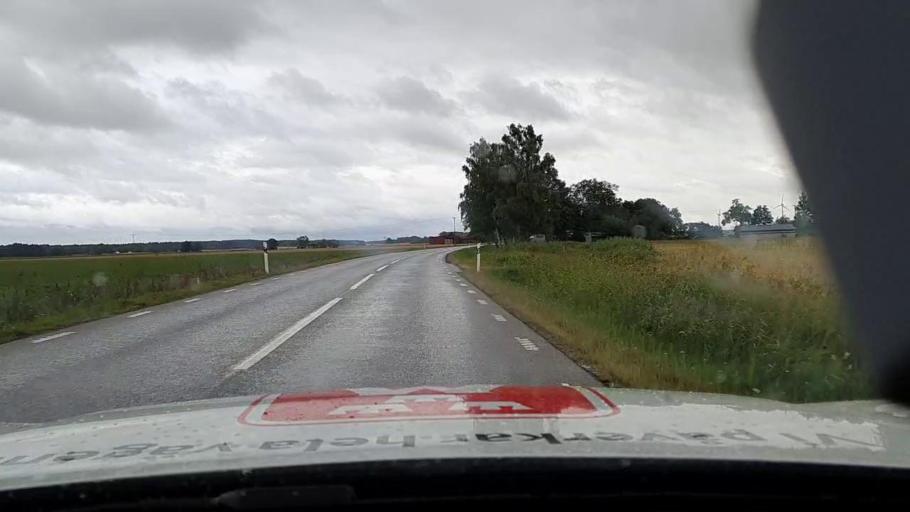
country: SE
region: Vaestra Goetaland
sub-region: Toreboda Kommun
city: Toereboda
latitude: 58.6216
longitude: 14.0138
